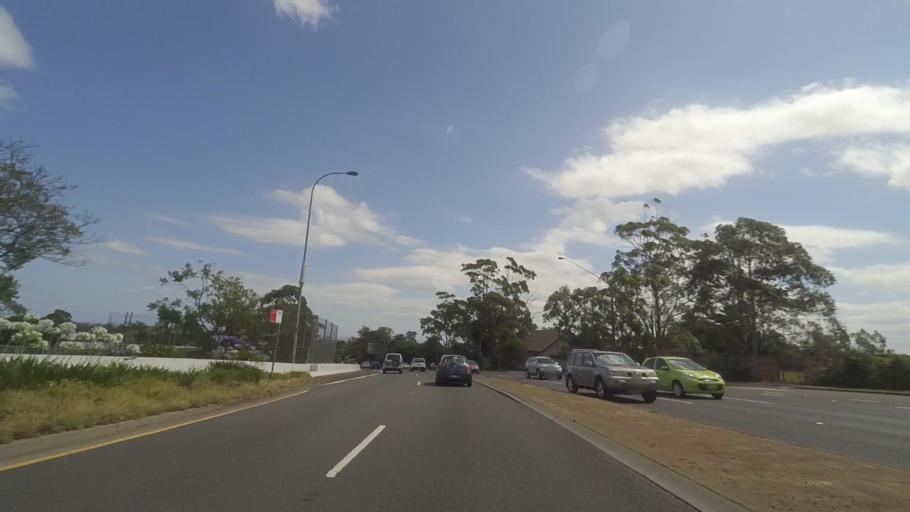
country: AU
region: New South Wales
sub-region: The Hills Shire
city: West Pennant
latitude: -33.7486
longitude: 151.0496
